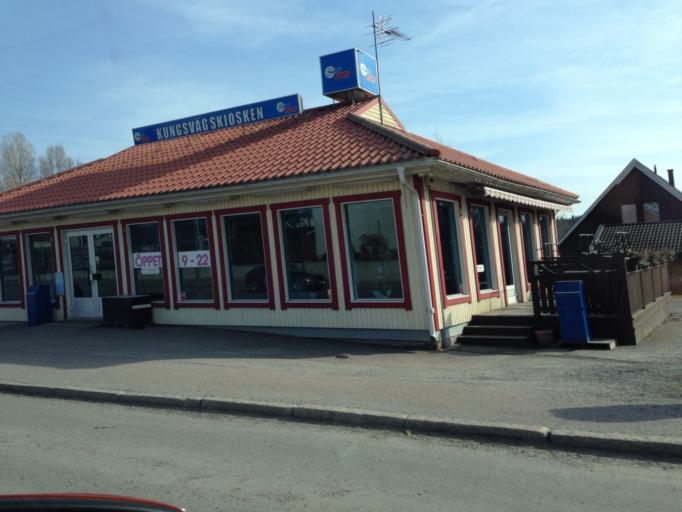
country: SE
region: Soedermanland
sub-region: Flens Kommun
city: Flen
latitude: 59.0535
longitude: 16.6054
